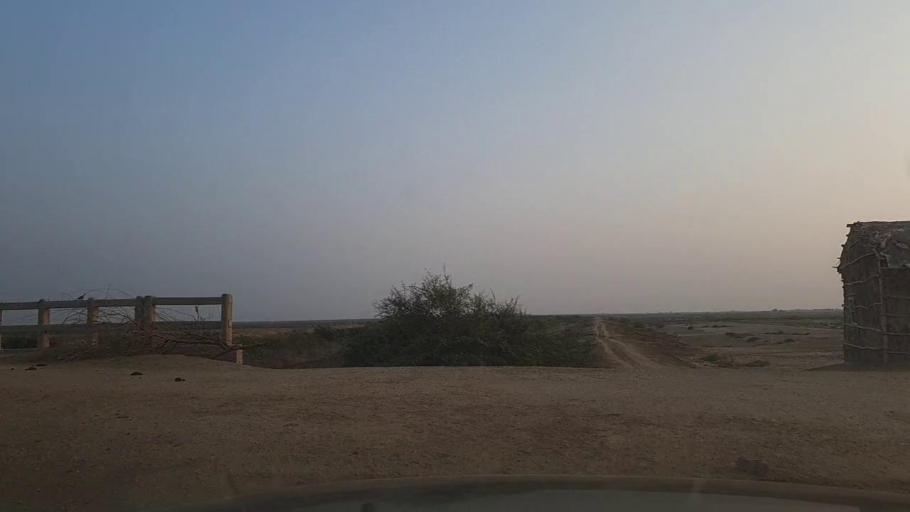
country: PK
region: Sindh
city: Jati
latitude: 24.5296
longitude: 68.4092
